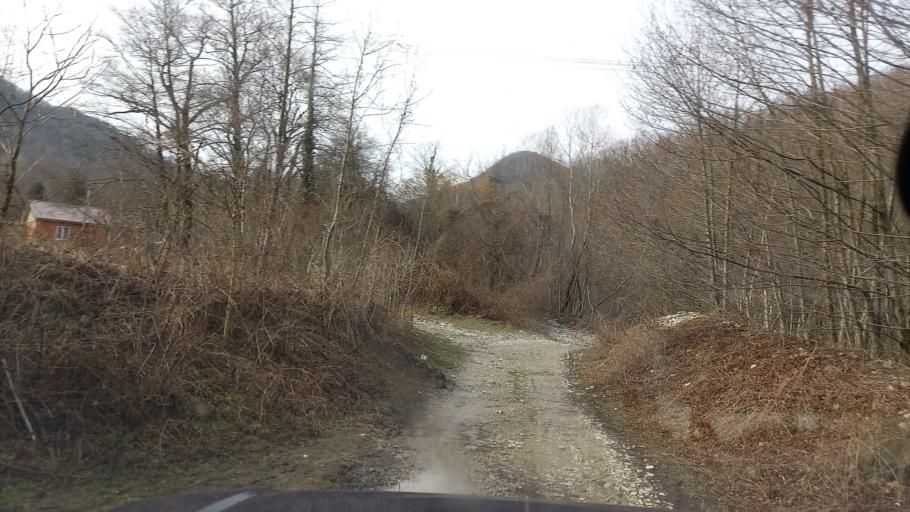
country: RU
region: Krasnodarskiy
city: Dzhubga
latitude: 44.4135
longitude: 38.7203
